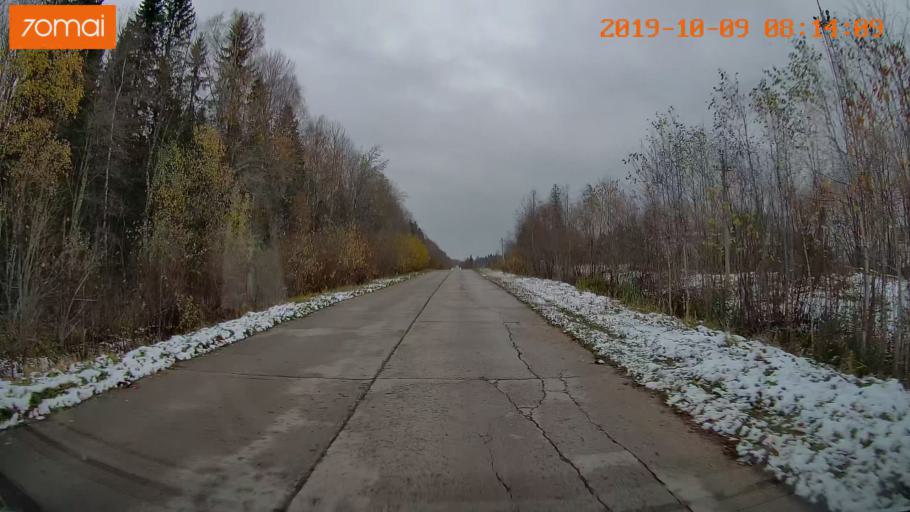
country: RU
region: Vologda
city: Gryazovets
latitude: 58.7271
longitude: 40.1510
